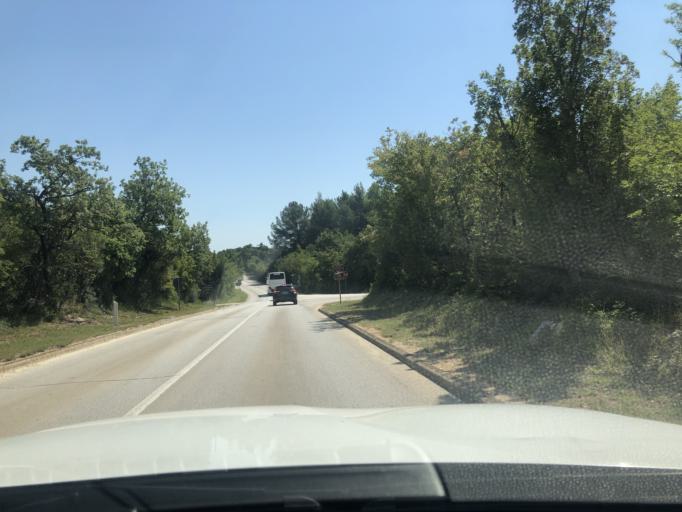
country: HR
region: Istarska
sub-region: Grad Rovinj
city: Rovinj
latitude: 45.0527
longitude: 13.7160
